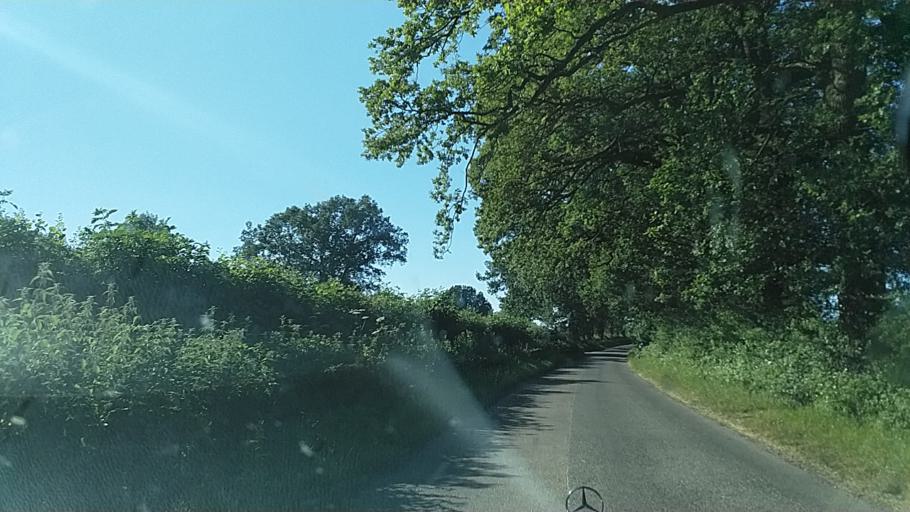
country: GB
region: England
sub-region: Warwickshire
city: Wroxall
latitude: 52.3240
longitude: -1.6464
